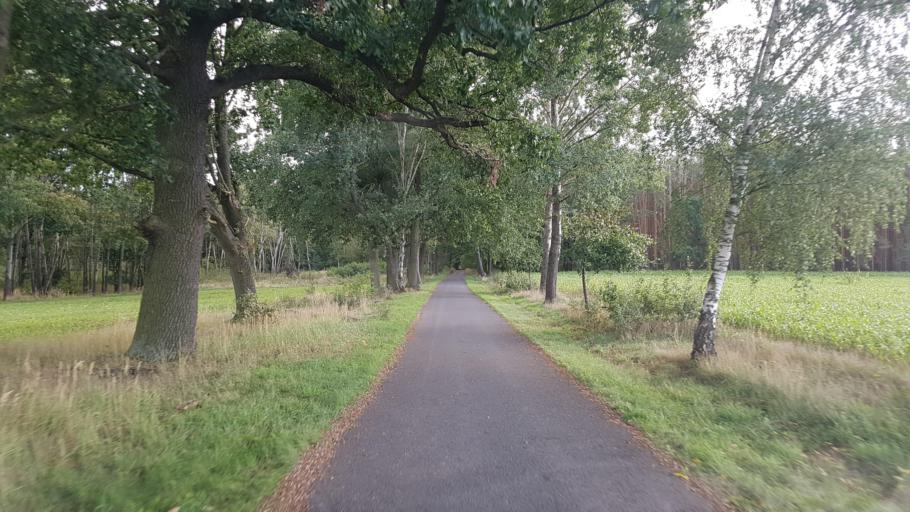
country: DE
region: Brandenburg
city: Ihlow
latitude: 51.8764
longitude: 13.2466
